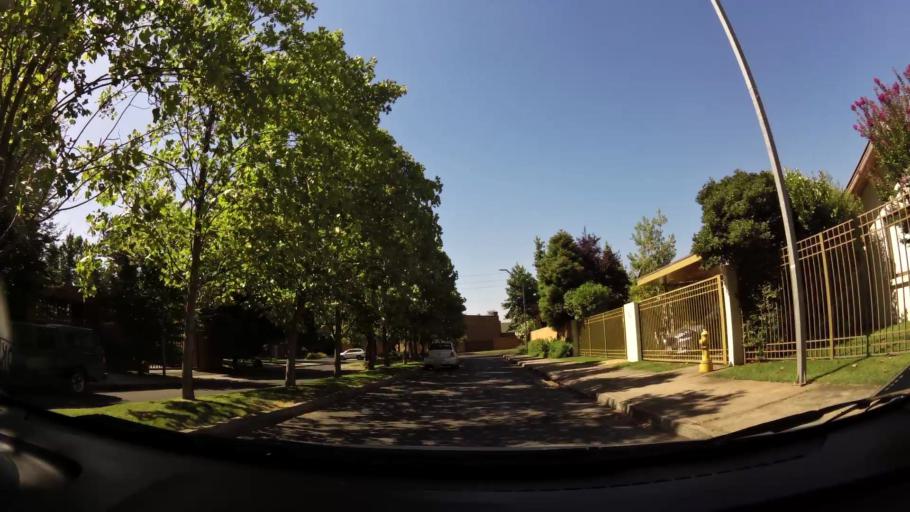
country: CL
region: Maule
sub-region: Provincia de Talca
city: Talca
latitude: -35.4356
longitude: -71.6159
